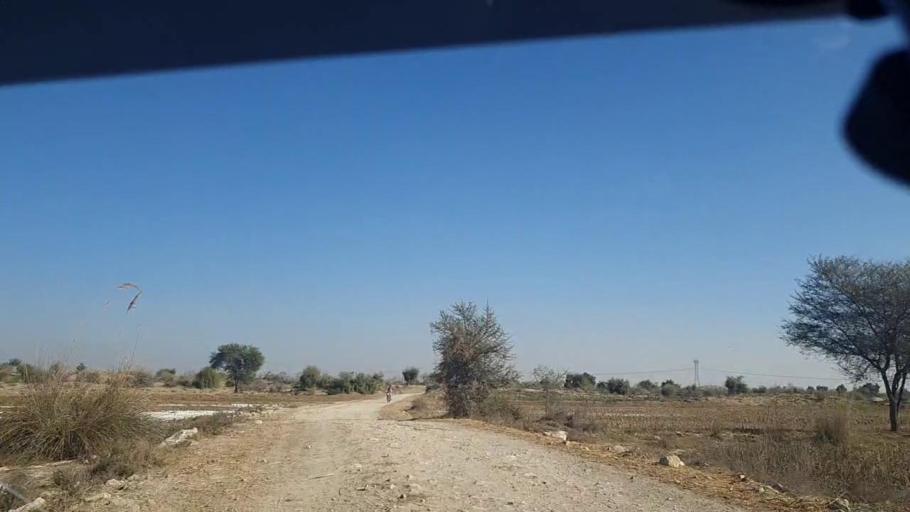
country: PK
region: Sindh
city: Khanpur
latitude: 27.6479
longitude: 69.3939
